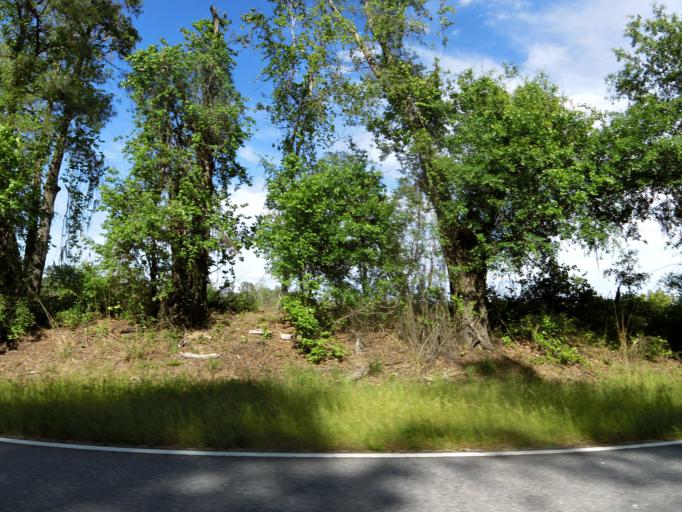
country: US
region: South Carolina
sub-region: Allendale County
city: Allendale
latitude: 33.1451
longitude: -81.1906
